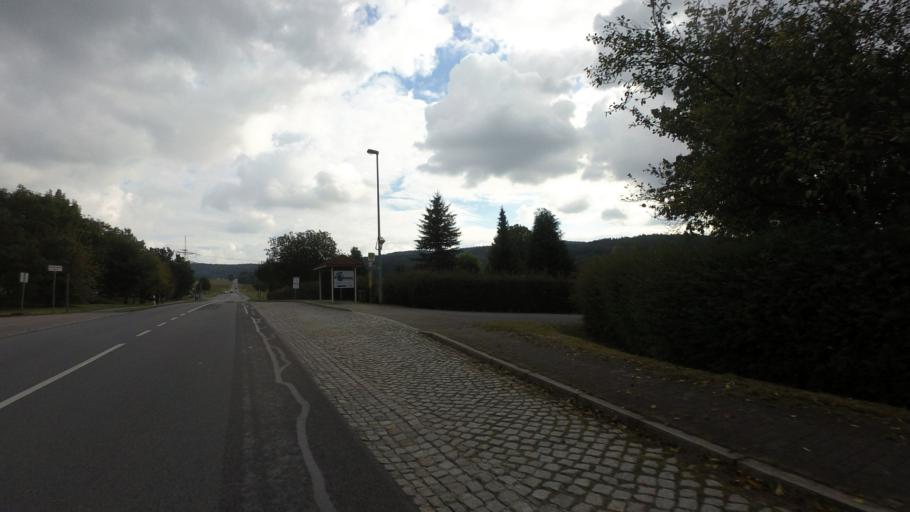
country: DE
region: Saxony
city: Crostau
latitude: 51.0948
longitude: 14.4740
